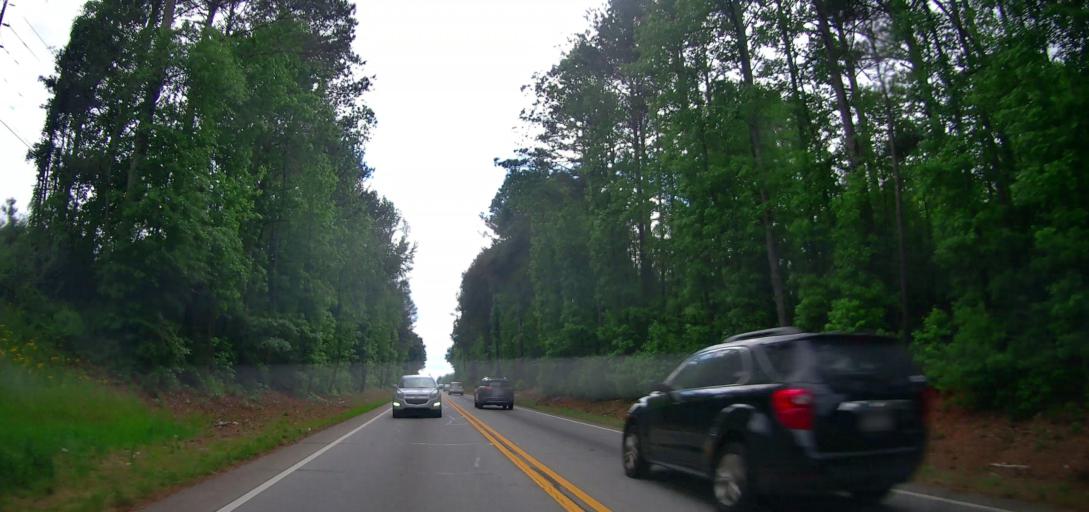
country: US
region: Georgia
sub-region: Walton County
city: Monroe
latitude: 33.7869
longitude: -83.7555
